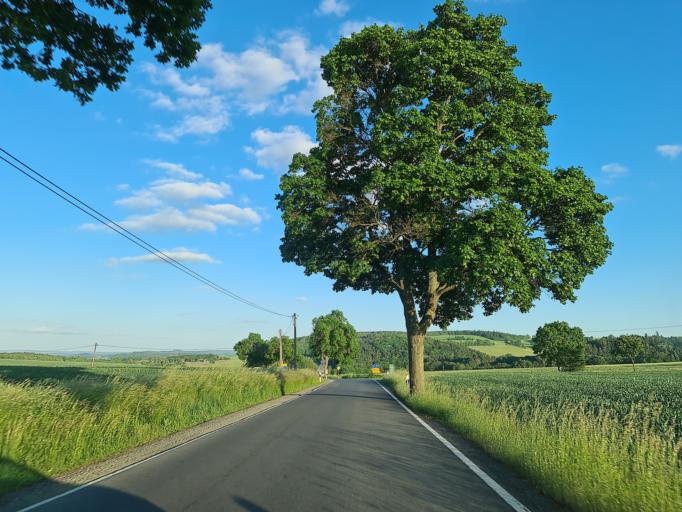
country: DE
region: Saxony
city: Reuth
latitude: 50.4641
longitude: 12.0135
